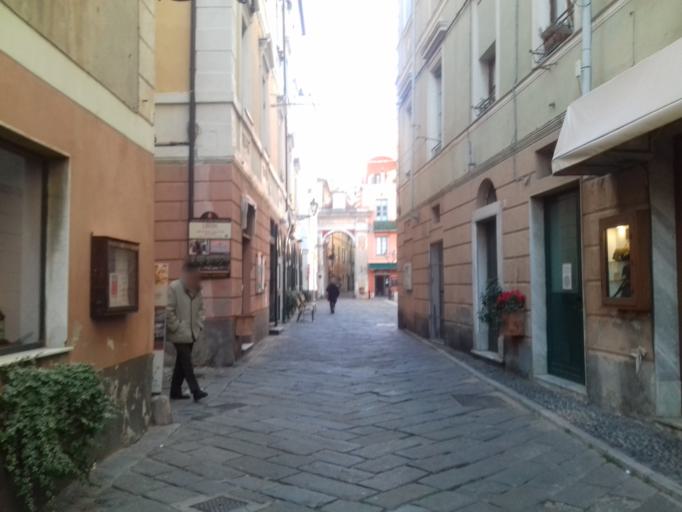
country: IT
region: Liguria
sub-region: Provincia di Savona
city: Finale Ligure
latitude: 44.1762
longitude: 8.3282
